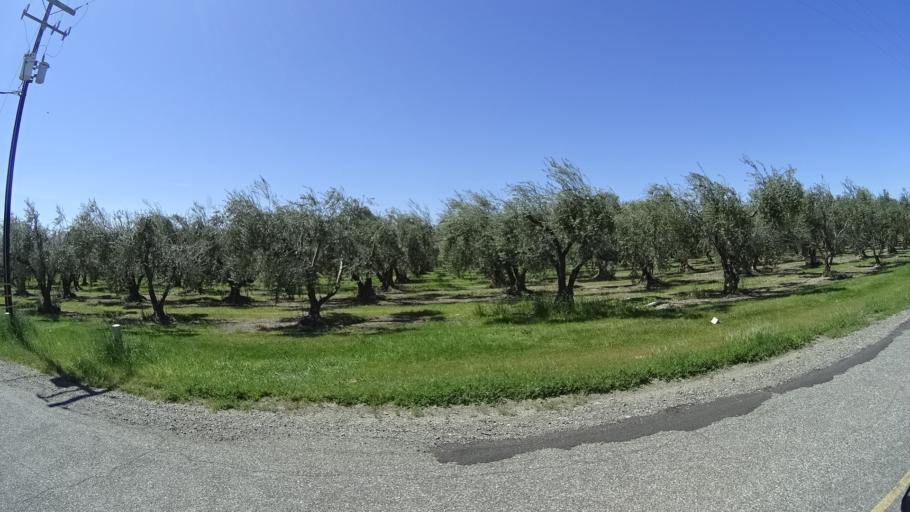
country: US
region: California
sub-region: Glenn County
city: Orland
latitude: 39.7440
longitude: -122.1595
